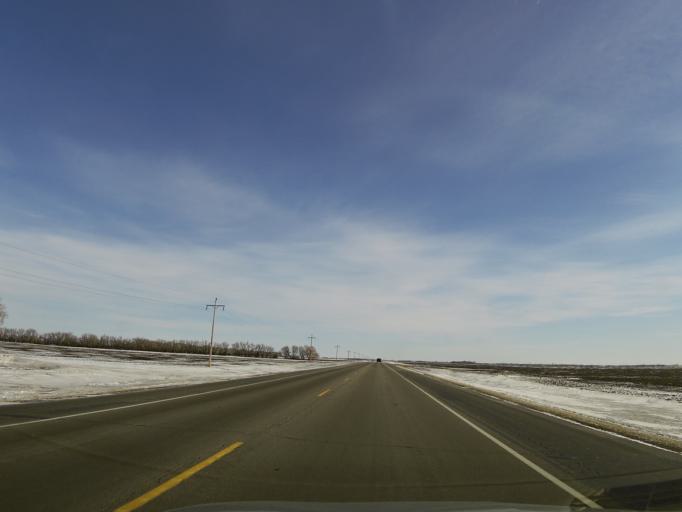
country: US
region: North Dakota
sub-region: Walsh County
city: Grafton
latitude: 48.4124
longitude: -97.3167
